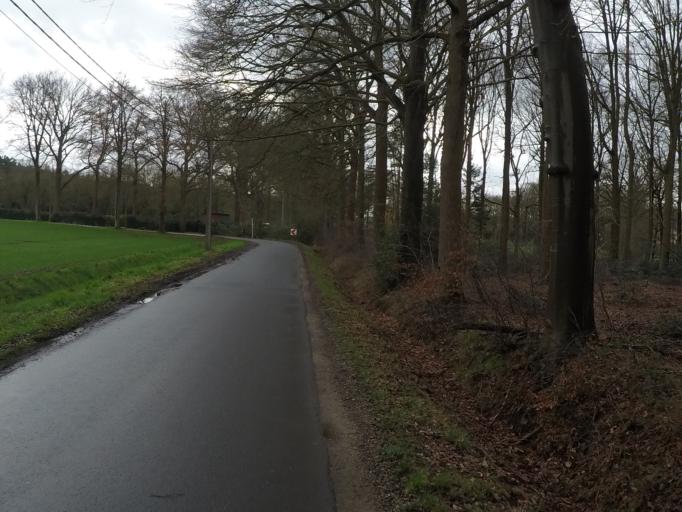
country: BE
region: Flanders
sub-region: Provincie Antwerpen
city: Zandhoven
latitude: 51.2168
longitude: 4.6474
